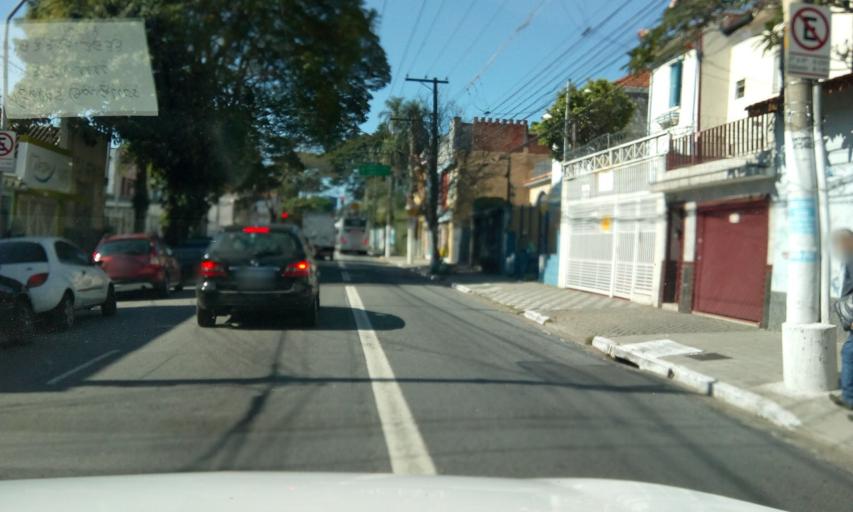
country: BR
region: Sao Paulo
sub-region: Guarulhos
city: Guarulhos
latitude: -23.5220
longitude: -46.5490
